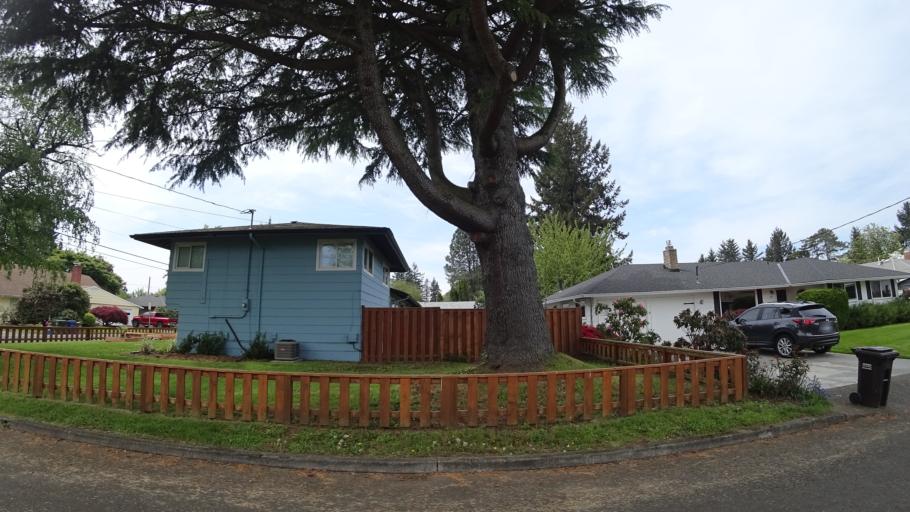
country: US
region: Oregon
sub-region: Clackamas County
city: Milwaukie
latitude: 45.4564
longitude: -122.6132
